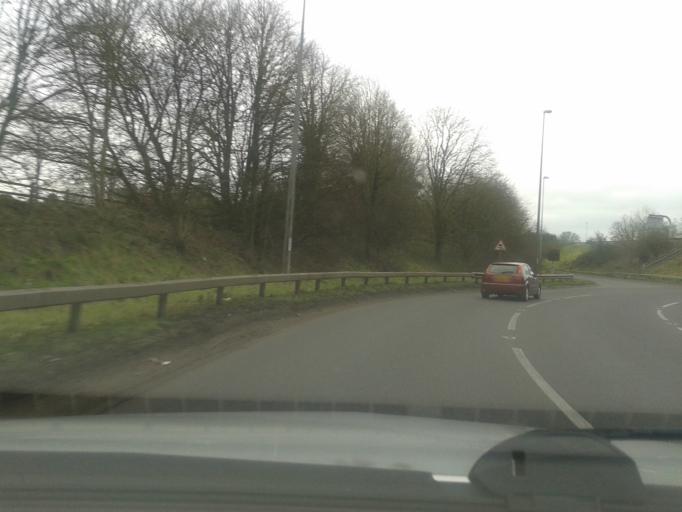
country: GB
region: England
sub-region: South Gloucestershire
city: Winterbourne
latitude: 51.5129
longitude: -2.5167
